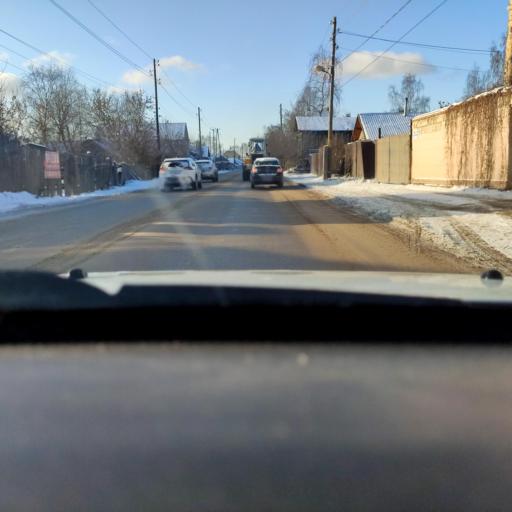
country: RU
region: Perm
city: Perm
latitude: 58.0336
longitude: 56.2459
